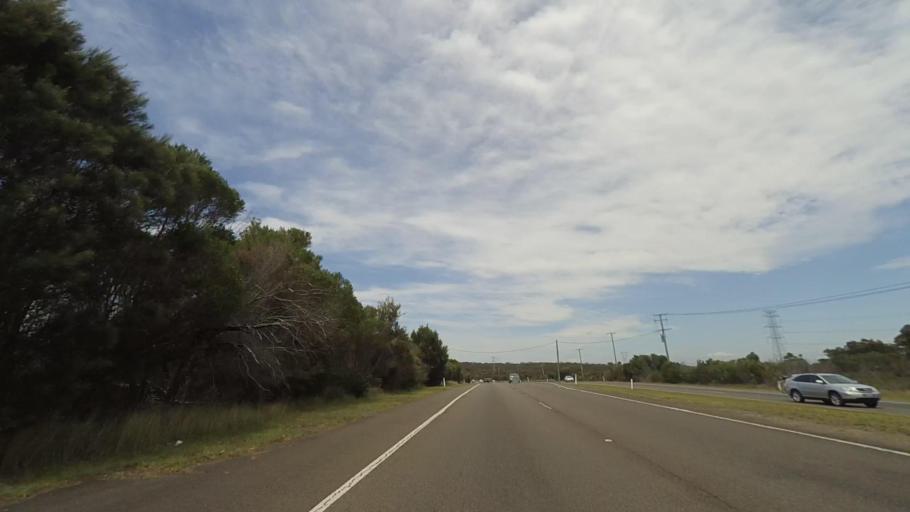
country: AU
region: New South Wales
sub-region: Sutherland Shire
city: Heathcote
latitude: -34.1118
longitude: 150.9930
